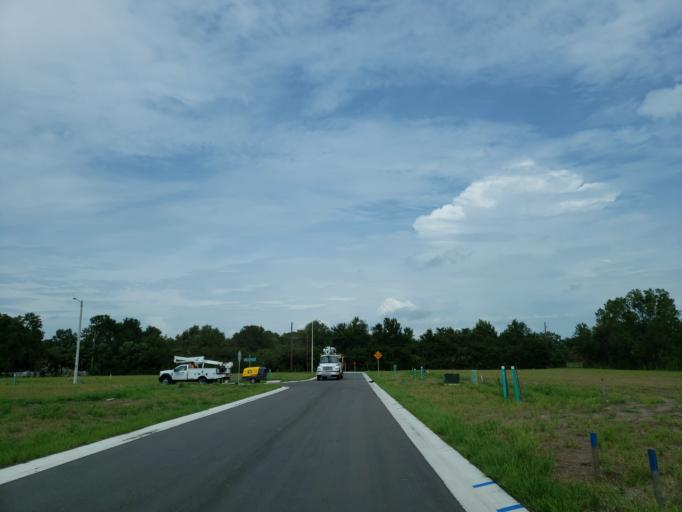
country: US
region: Florida
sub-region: Hillsborough County
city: Gibsonton
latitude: 27.8327
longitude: -82.3582
